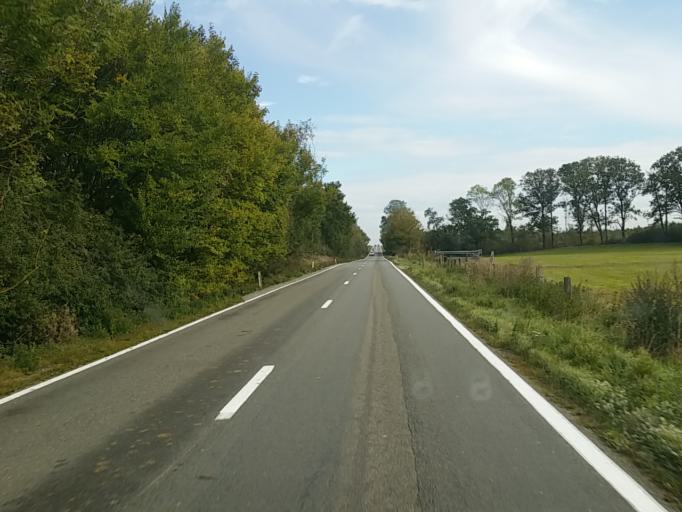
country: BE
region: Wallonia
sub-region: Province du Luxembourg
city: Etalle
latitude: 49.6951
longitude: 5.6161
